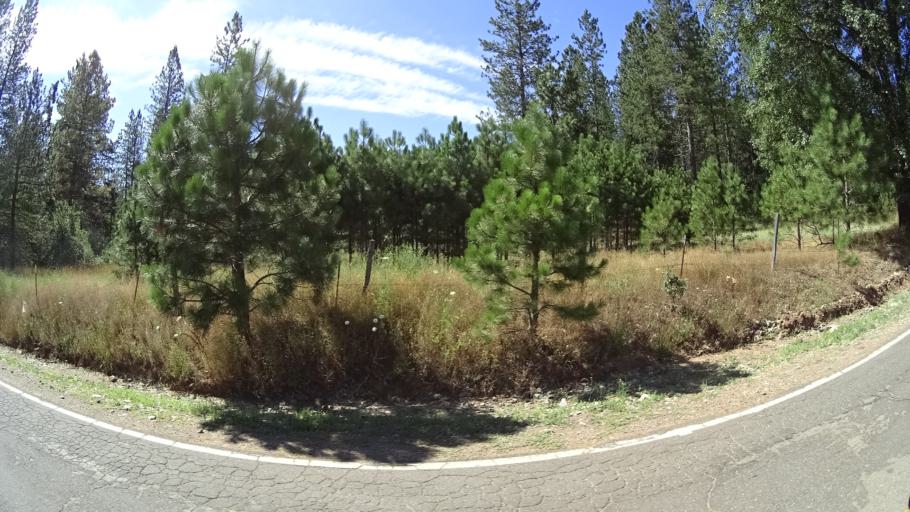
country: US
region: California
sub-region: Amador County
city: Pioneer
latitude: 38.3421
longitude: -120.5128
